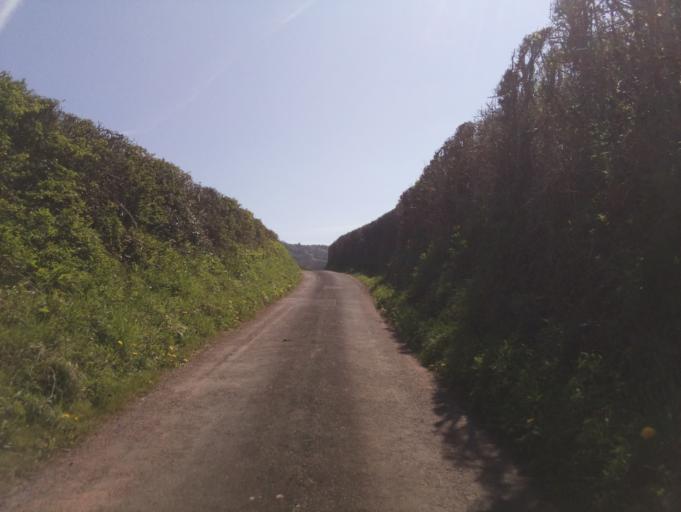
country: GB
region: Wales
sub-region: Monmouthshire
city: Llangwm
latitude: 51.6913
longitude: -2.8237
